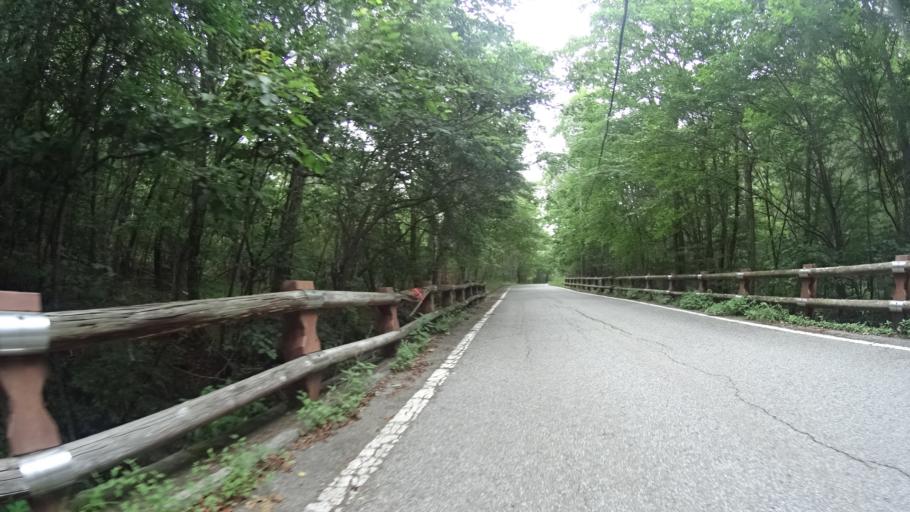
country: JP
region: Yamanashi
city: Nirasaki
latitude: 35.8907
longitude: 138.5672
